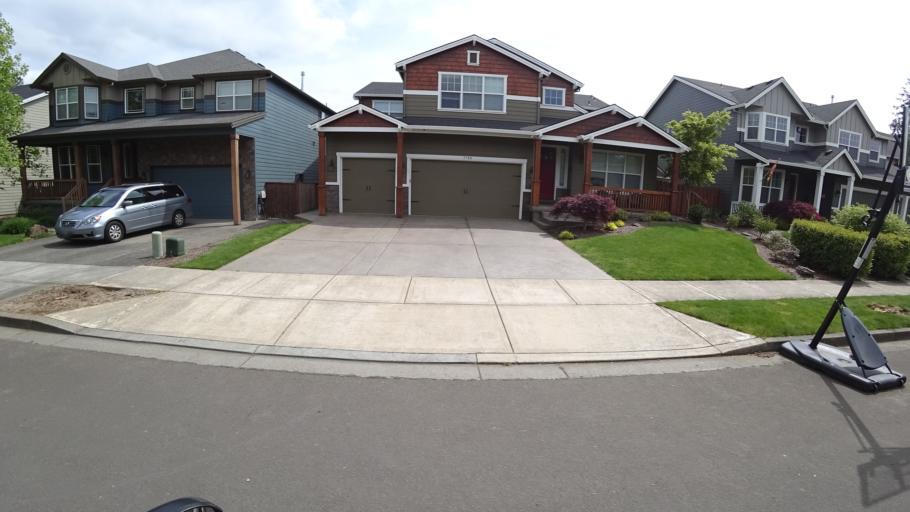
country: US
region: Oregon
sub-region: Washington County
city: Hillsboro
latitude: 45.5475
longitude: -122.9989
